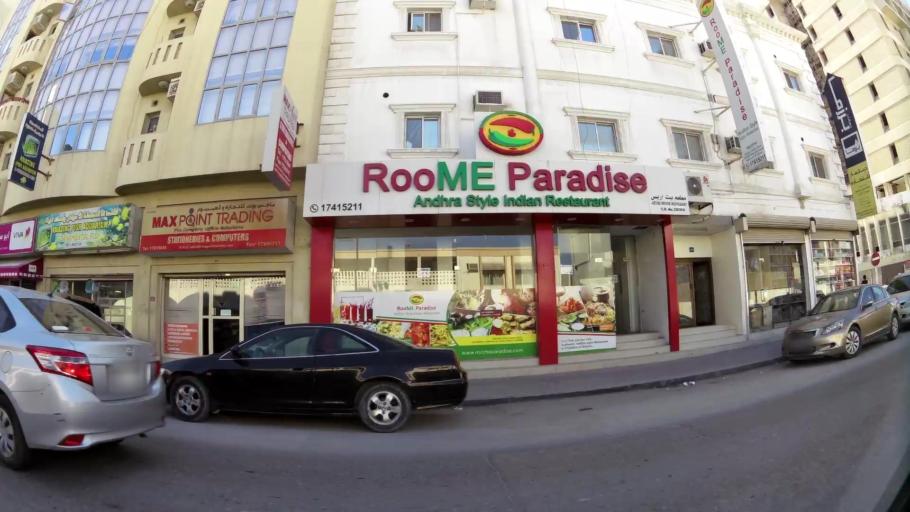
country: BH
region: Manama
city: Manama
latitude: 26.2253
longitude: 50.5833
